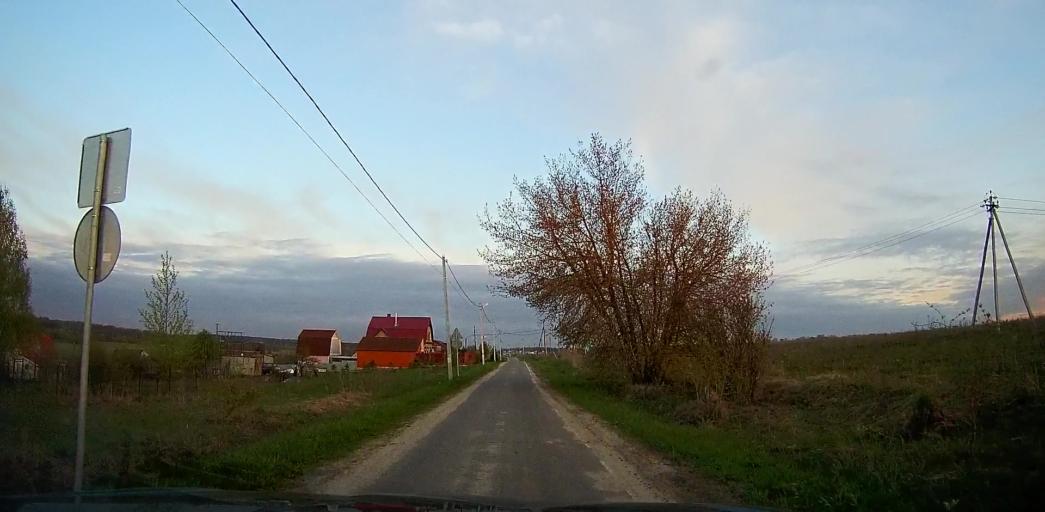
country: RU
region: Moskovskaya
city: Peski
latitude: 55.2294
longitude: 38.7335
